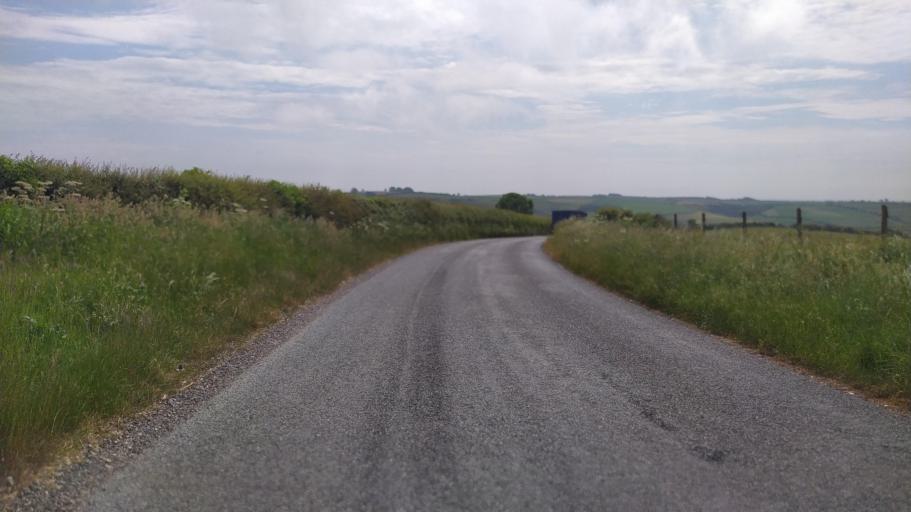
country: GB
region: England
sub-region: Dorset
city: Dorchester
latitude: 50.8001
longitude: -2.5410
